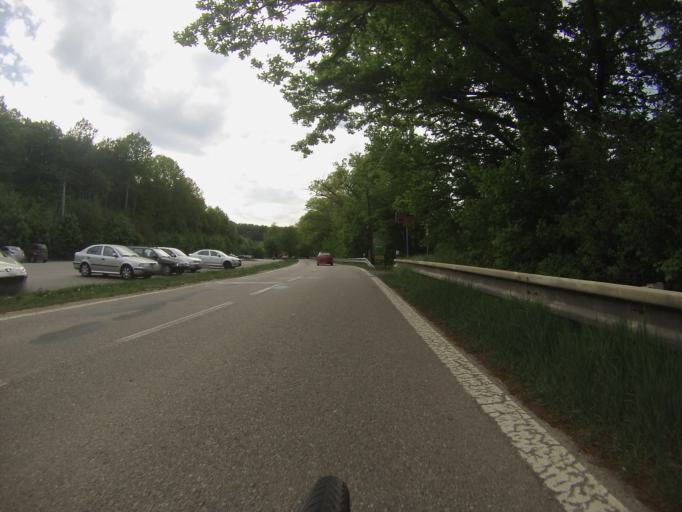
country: CZ
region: South Moravian
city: Veverska Bityska
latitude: 49.2477
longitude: 16.4934
